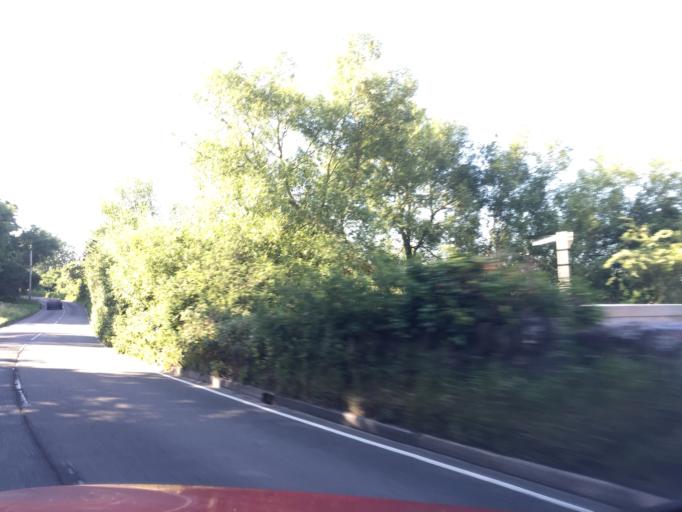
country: GB
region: England
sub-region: South Gloucestershire
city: Siston
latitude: 51.4667
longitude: -2.4691
